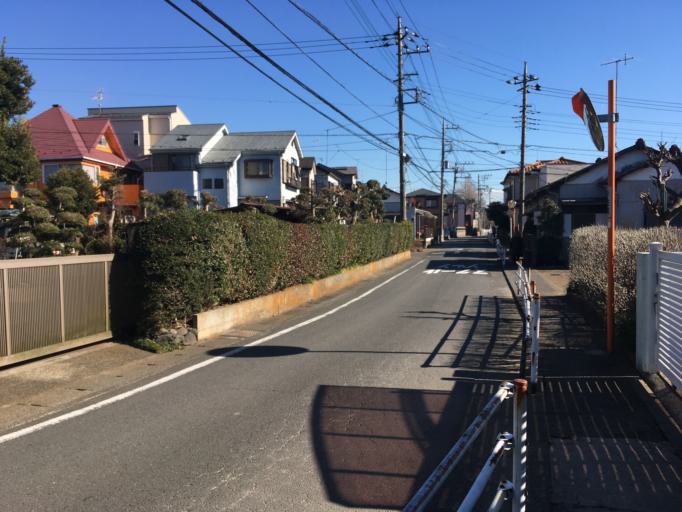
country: JP
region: Kanagawa
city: Minami-rinkan
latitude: 35.4618
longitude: 139.4687
